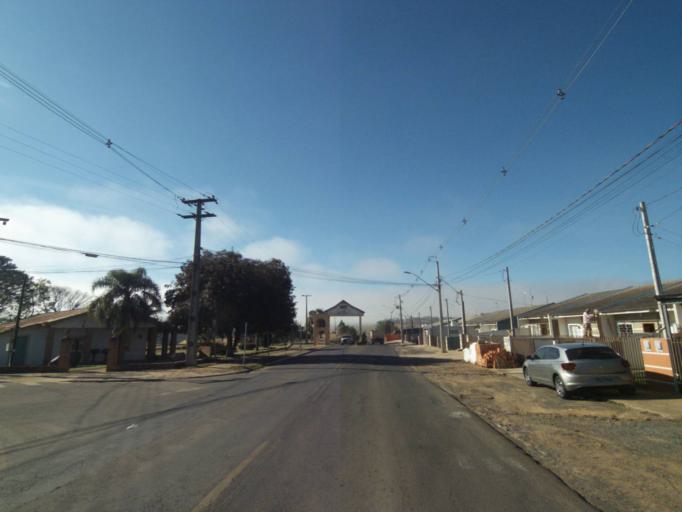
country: BR
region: Parana
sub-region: Tibagi
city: Tibagi
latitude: -24.5266
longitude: -50.4013
